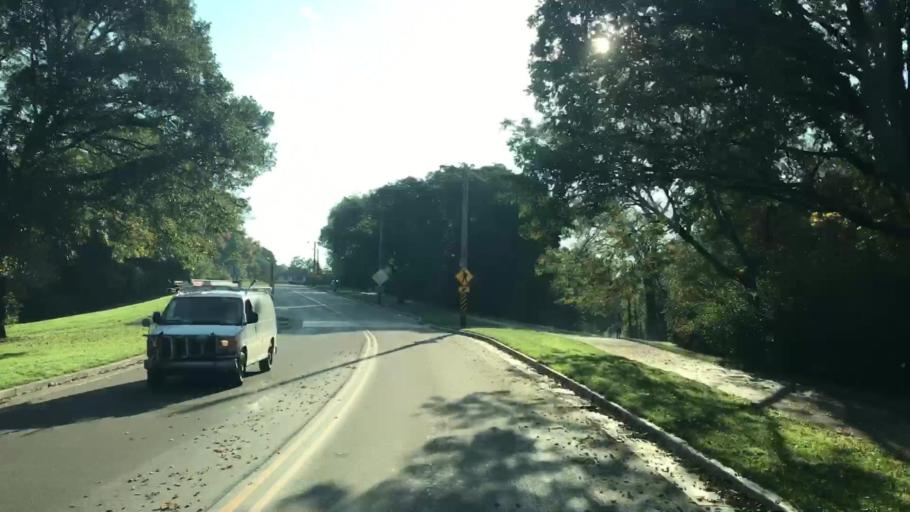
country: US
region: Wisconsin
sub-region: Milwaukee County
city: Wauwatosa
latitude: 43.0507
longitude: -88.0133
